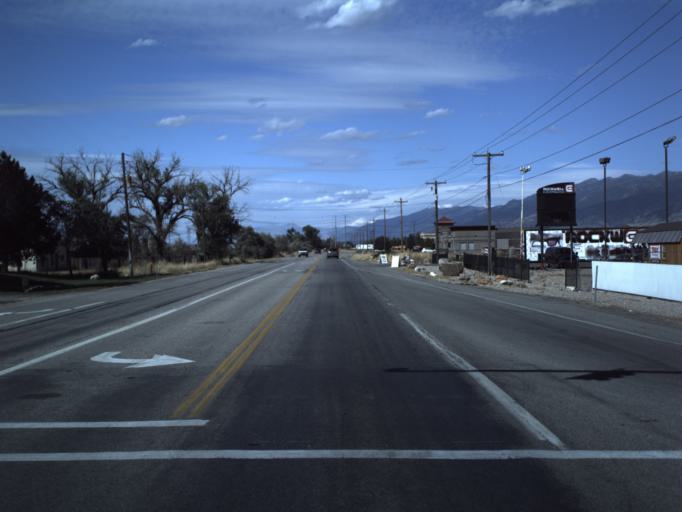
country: US
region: Utah
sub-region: Davis County
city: West Bountiful
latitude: 40.8747
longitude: -111.9300
